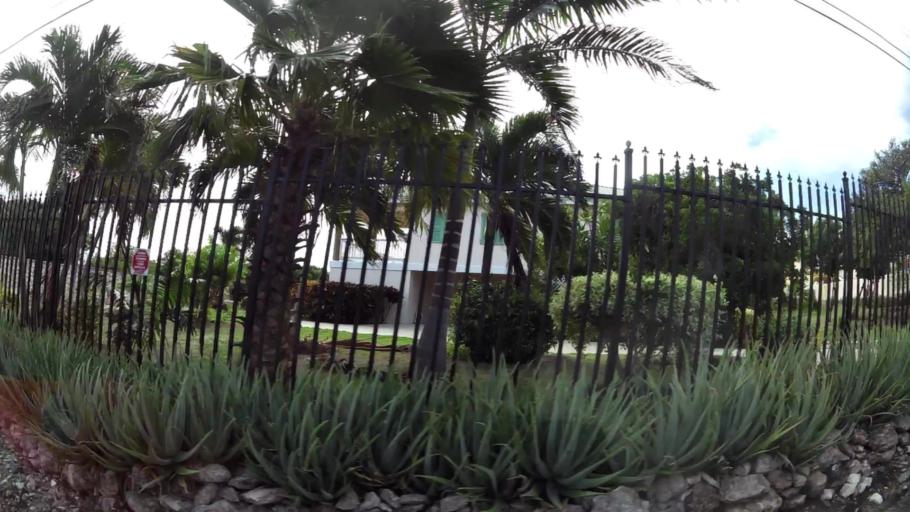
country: AG
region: Saint Peter
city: Parham
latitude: 17.1004
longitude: -61.6866
